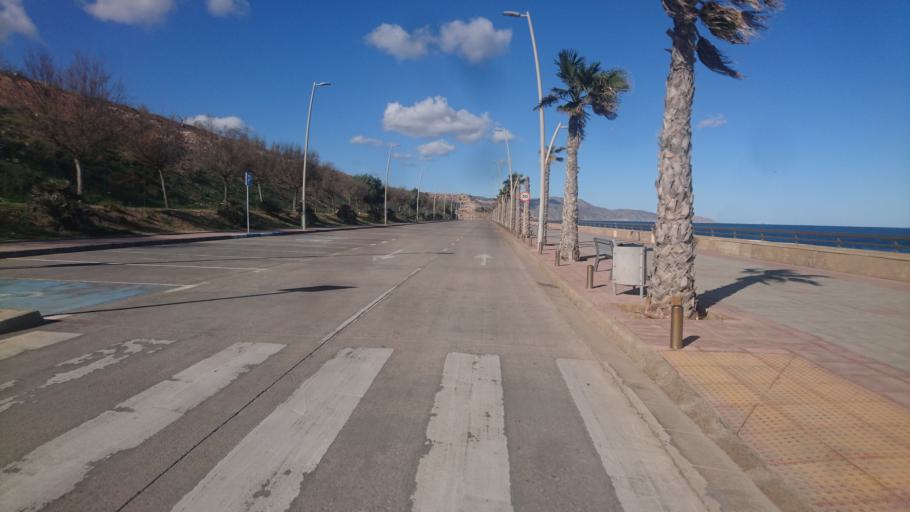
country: ES
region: Melilla
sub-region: Melilla
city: Melilla
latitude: 35.2999
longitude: -2.9364
